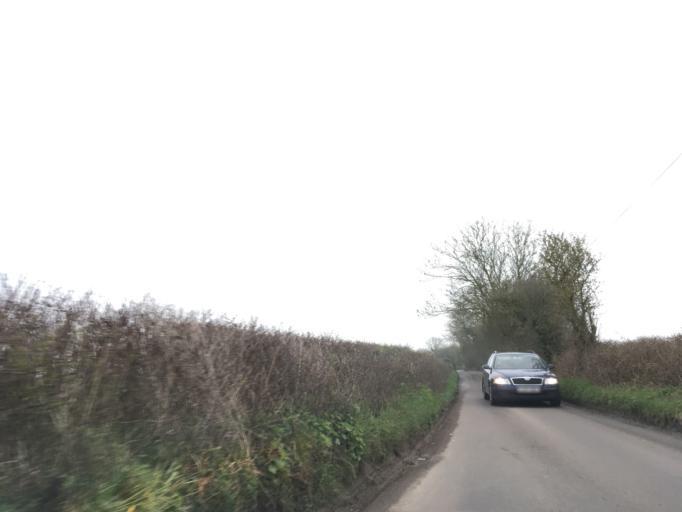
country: GB
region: England
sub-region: South Gloucestershire
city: Alveston
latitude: 51.5575
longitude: -2.5326
